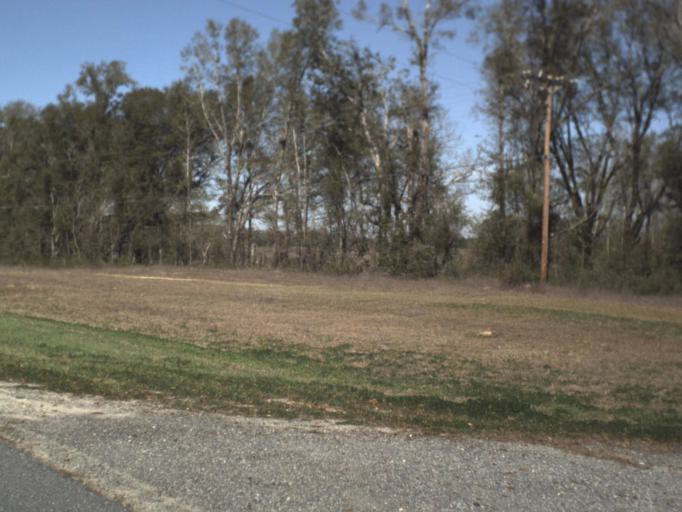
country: US
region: Florida
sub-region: Jackson County
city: Marianna
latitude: 30.7353
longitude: -85.1020
